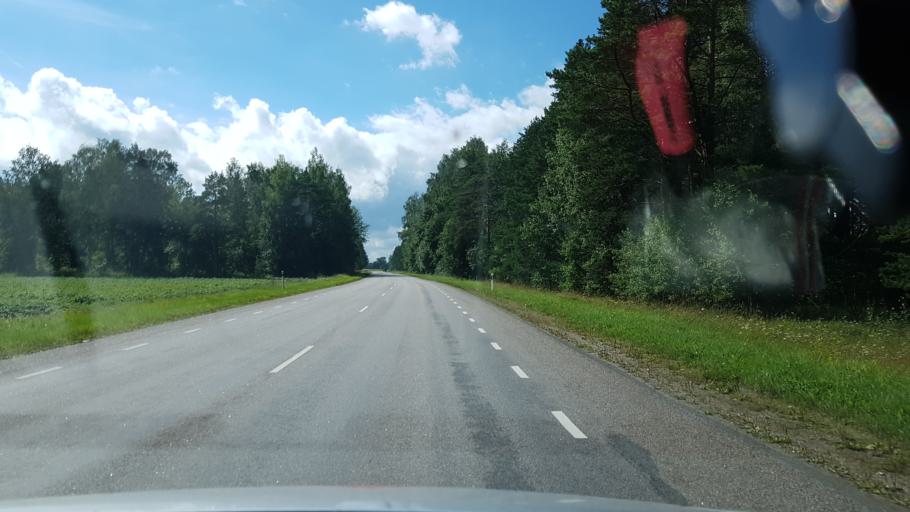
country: EE
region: Ida-Virumaa
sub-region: Puessi linn
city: Pussi
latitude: 59.3677
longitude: 27.0240
